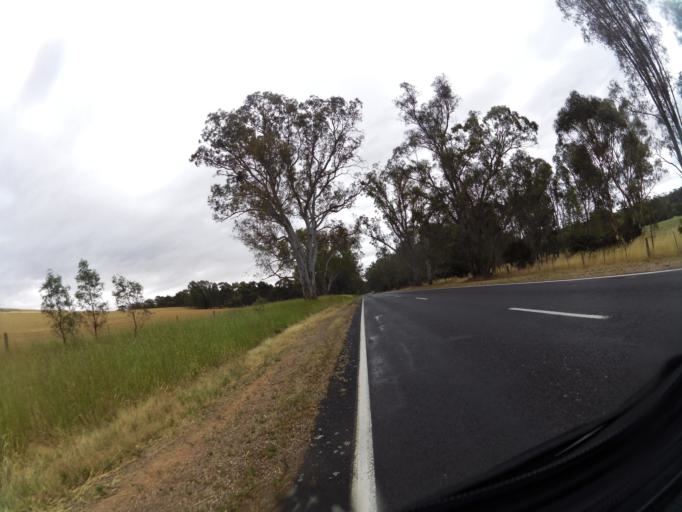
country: AU
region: Victoria
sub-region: Mount Alexander
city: Castlemaine
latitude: -37.1505
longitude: 144.0412
